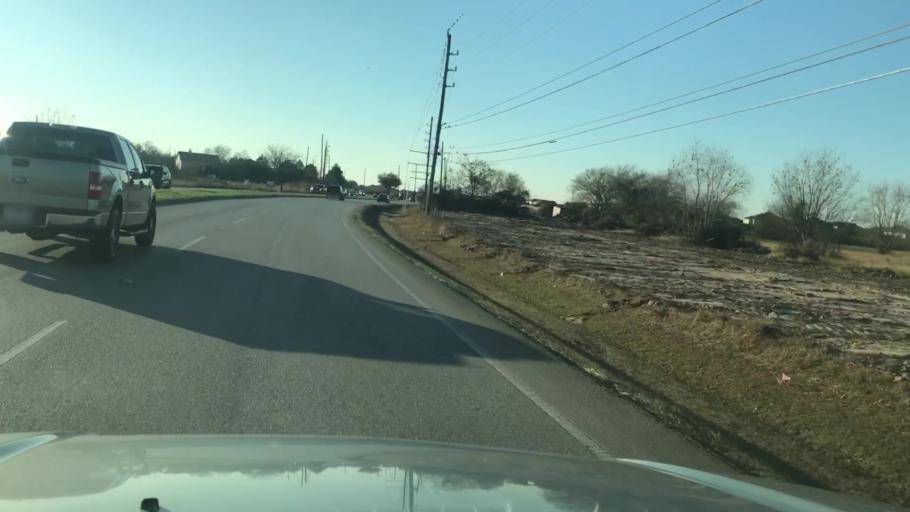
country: US
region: Texas
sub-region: Fort Bend County
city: Cinco Ranch
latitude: 29.8313
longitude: -95.7376
